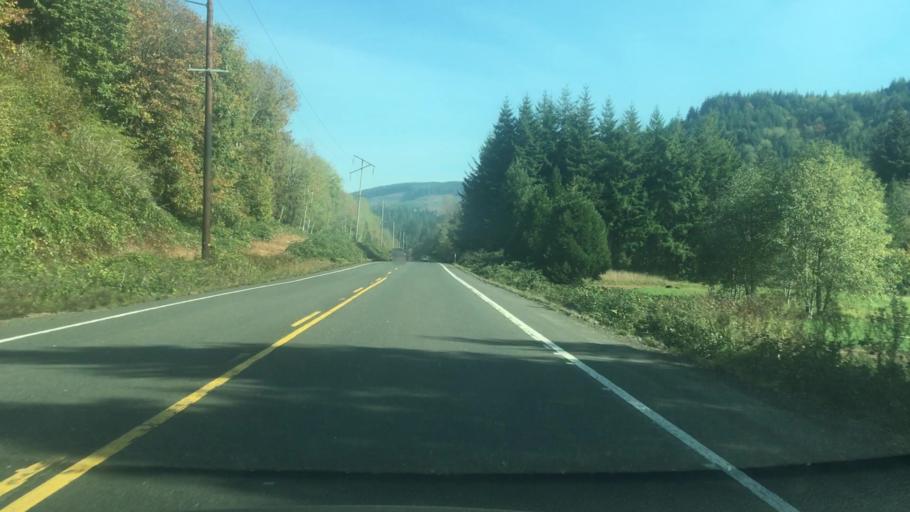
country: US
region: Oregon
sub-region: Lincoln County
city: Rose Lodge
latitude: 45.0219
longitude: -123.8429
